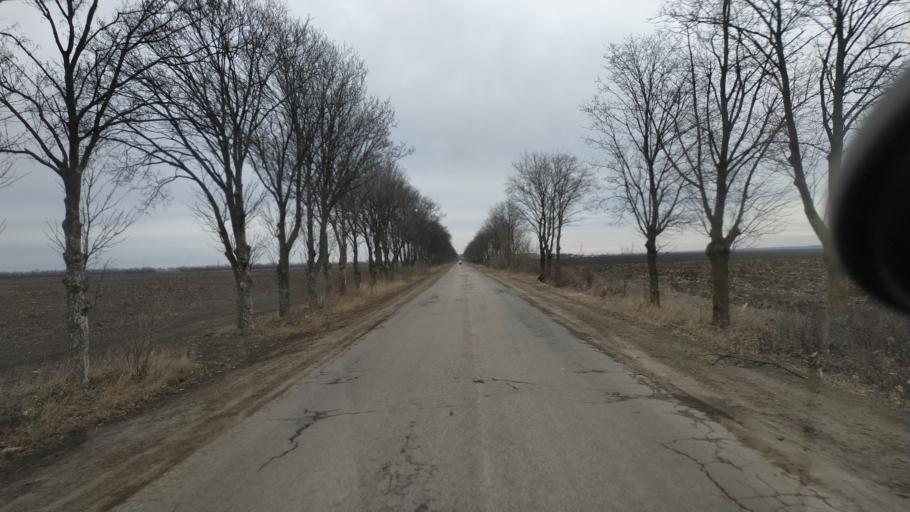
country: MD
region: Telenesti
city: Cocieri
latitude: 47.2660
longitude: 29.0889
